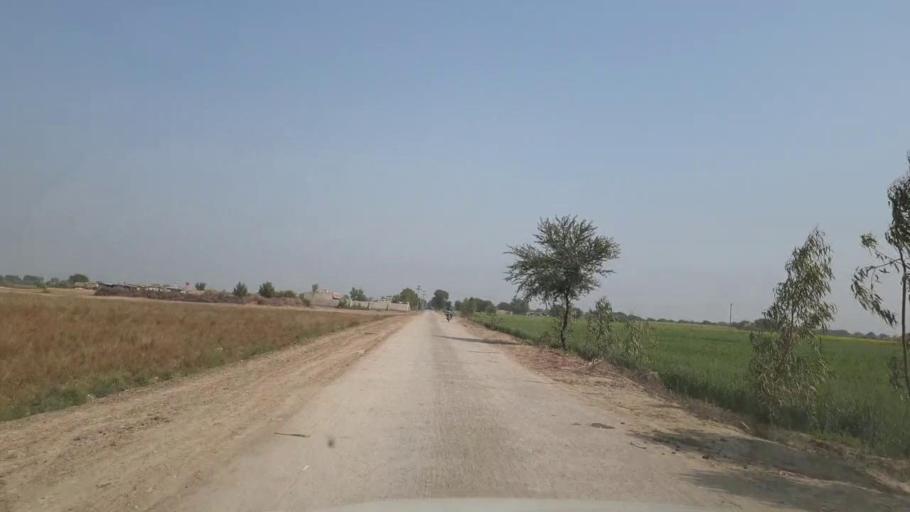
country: PK
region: Sindh
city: Mirpur Khas
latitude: 25.6633
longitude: 69.1695
